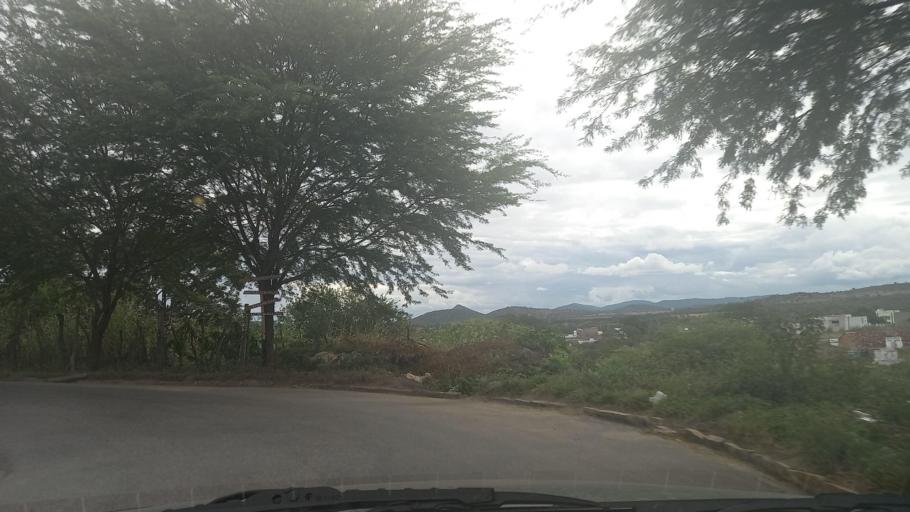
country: BR
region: Pernambuco
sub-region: Caruaru
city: Caruaru
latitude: -8.2898
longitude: -36.0303
